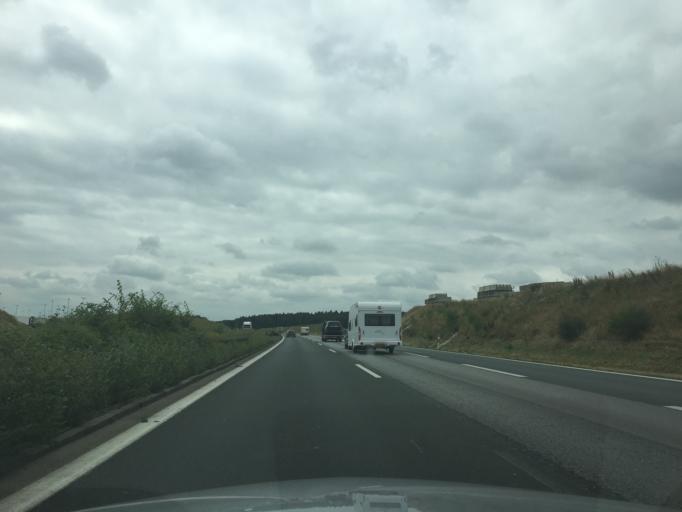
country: DE
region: Bavaria
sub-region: Regierungsbezirk Mittelfranken
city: Herzogenaurach
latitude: 49.5854
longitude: 10.9268
